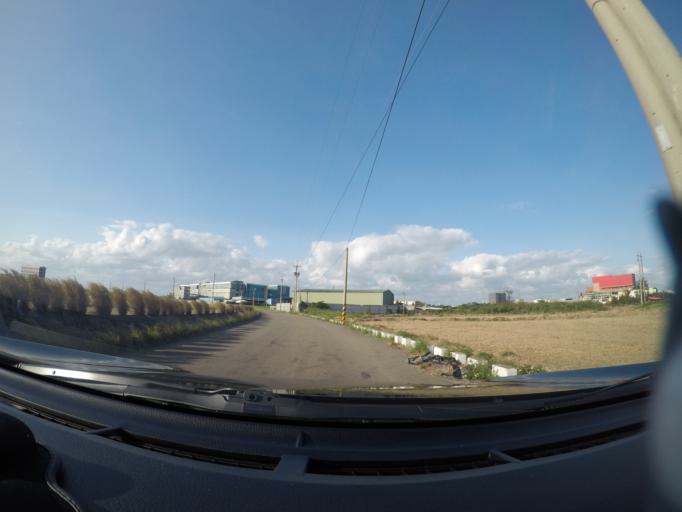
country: TW
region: Taiwan
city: Taoyuan City
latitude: 25.1049
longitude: 121.2523
